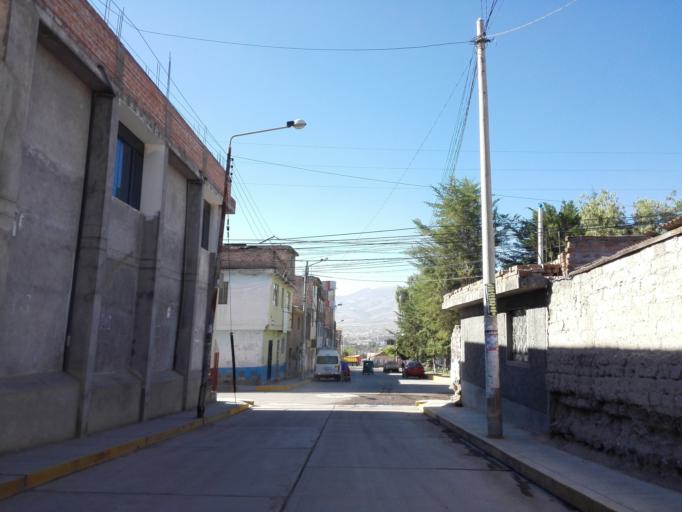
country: PE
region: Ayacucho
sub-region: Provincia de Huamanga
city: Ayacucho
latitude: -13.1538
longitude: -74.2157
